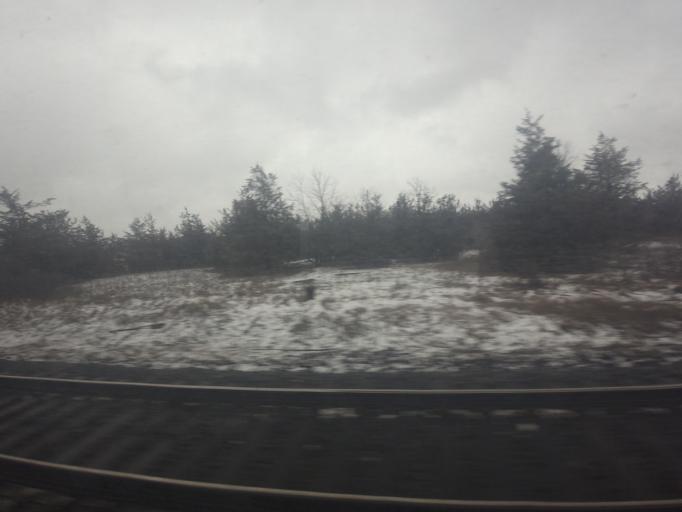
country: CA
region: Ontario
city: Deseronto
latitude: 44.2129
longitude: -77.1875
